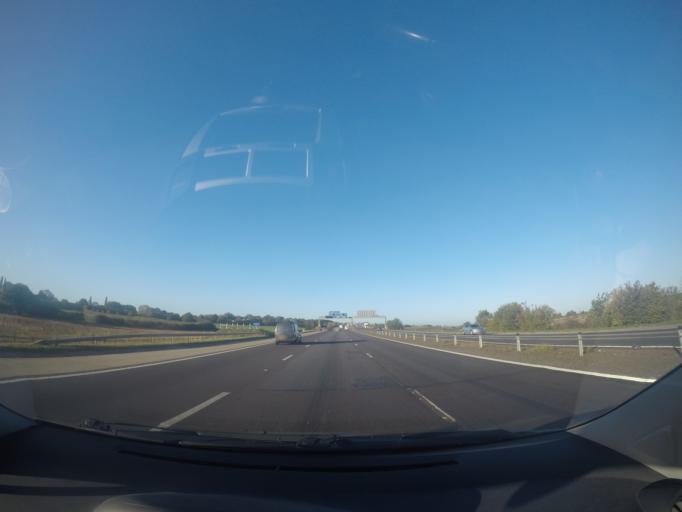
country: GB
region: England
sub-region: City and Borough of Leeds
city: Garforth
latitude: 53.8029
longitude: -1.3928
